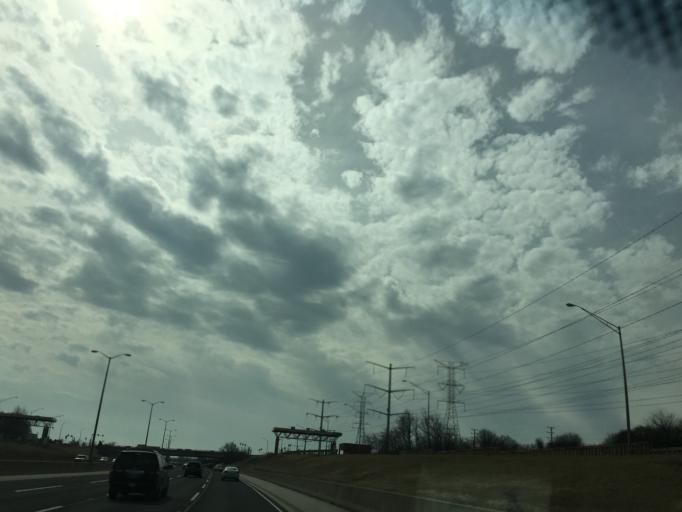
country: US
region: Illinois
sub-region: DuPage County
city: Lisle
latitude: 41.7895
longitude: -88.0568
